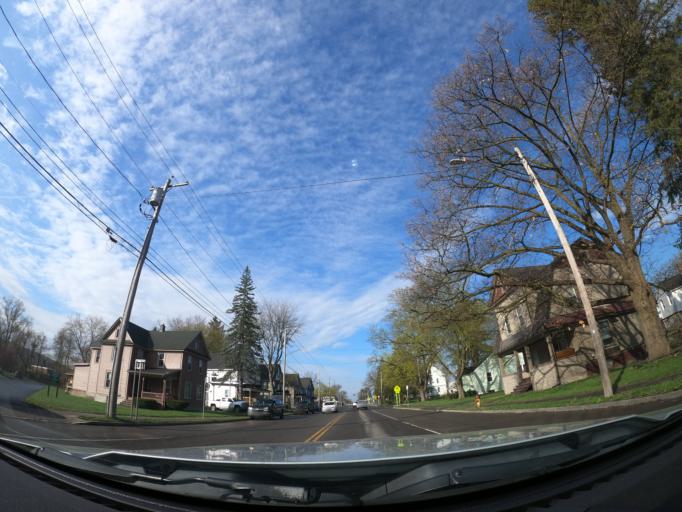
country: US
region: New York
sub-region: Cortland County
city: Cortland
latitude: 42.5896
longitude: -76.1933
